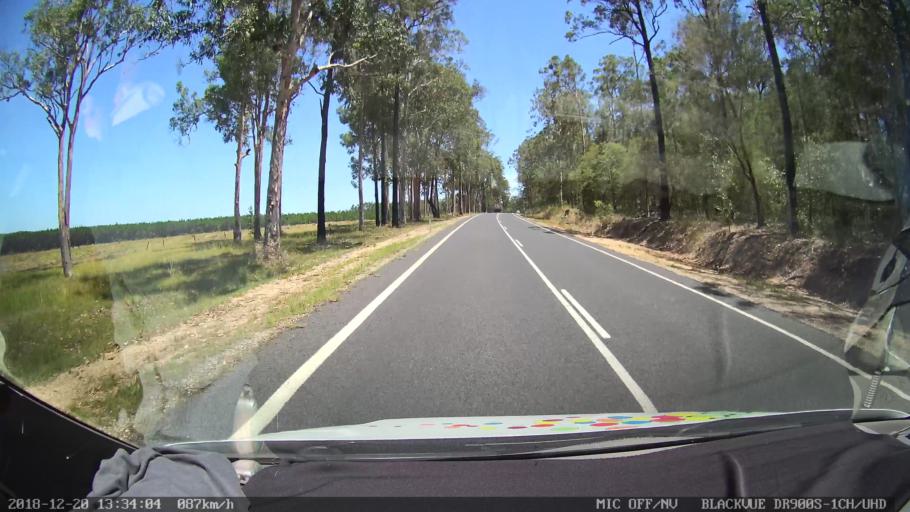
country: AU
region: New South Wales
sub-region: Clarence Valley
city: Gordon
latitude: -29.2539
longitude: 152.9847
